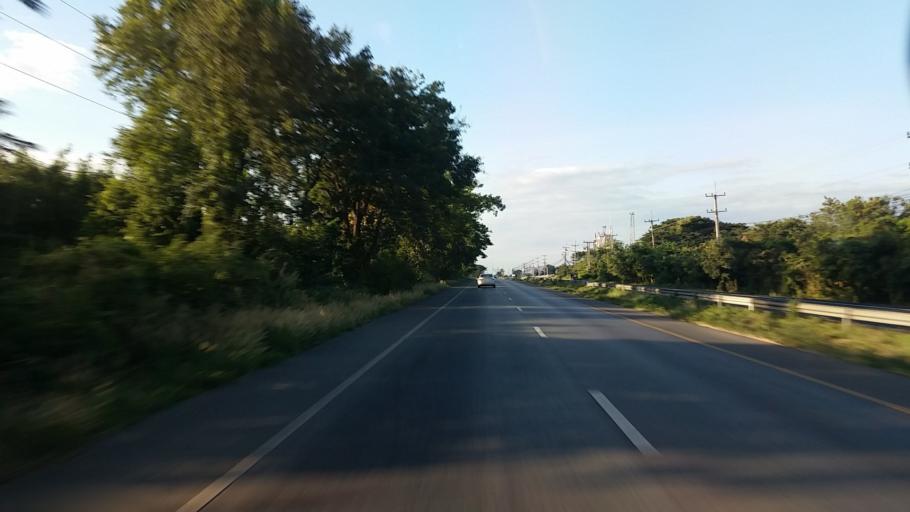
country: TH
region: Lop Buri
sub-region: Amphoe Tha Luang
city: Tha Luang
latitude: 15.0978
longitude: 101.0179
